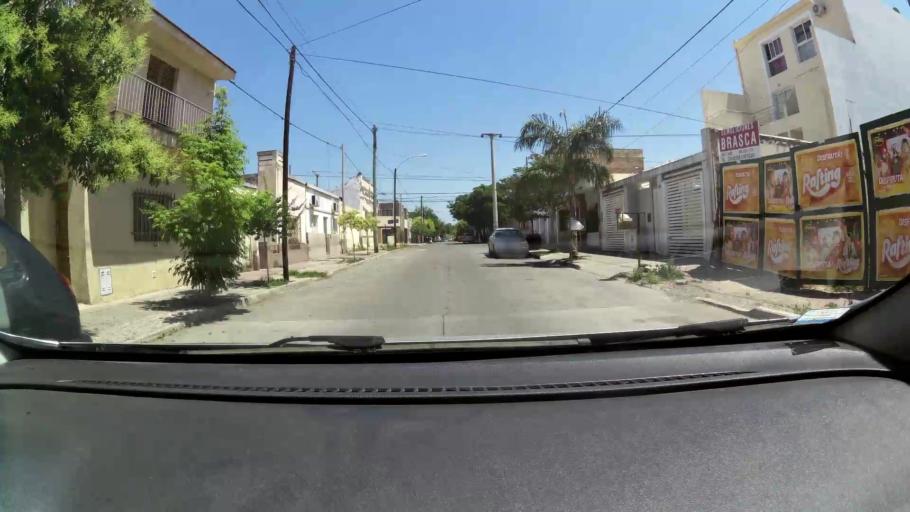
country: AR
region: Cordoba
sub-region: Departamento de Capital
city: Cordoba
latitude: -31.4003
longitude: -64.1996
